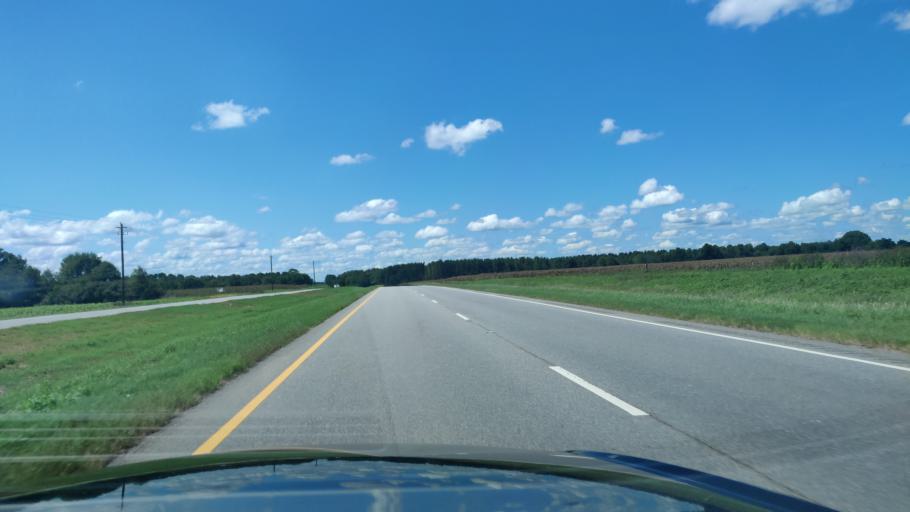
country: US
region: Georgia
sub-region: Terrell County
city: Dawson
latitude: 31.8469
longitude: -84.4727
